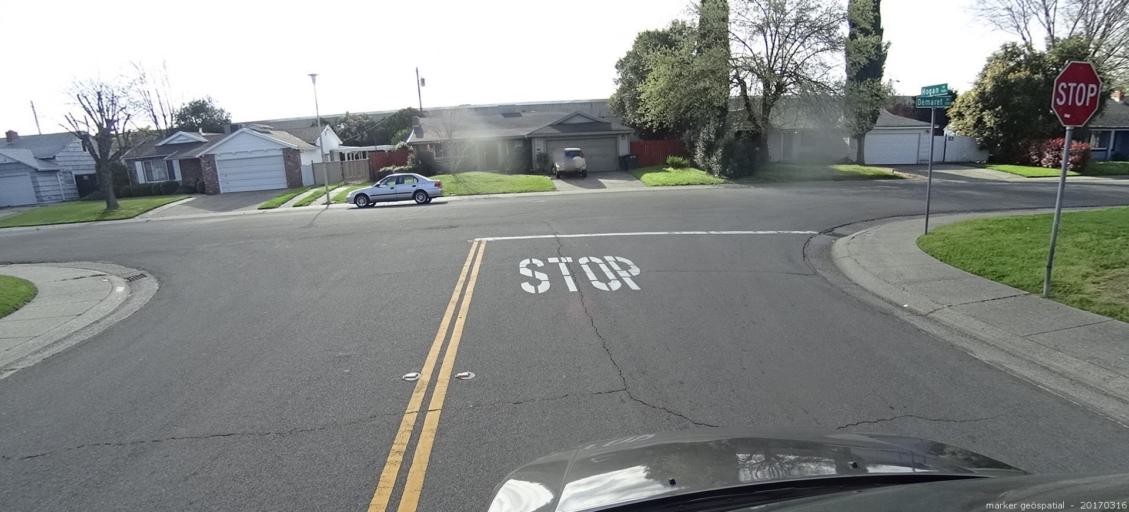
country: US
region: California
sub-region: Sacramento County
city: Parkway
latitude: 38.4976
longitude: -121.4852
